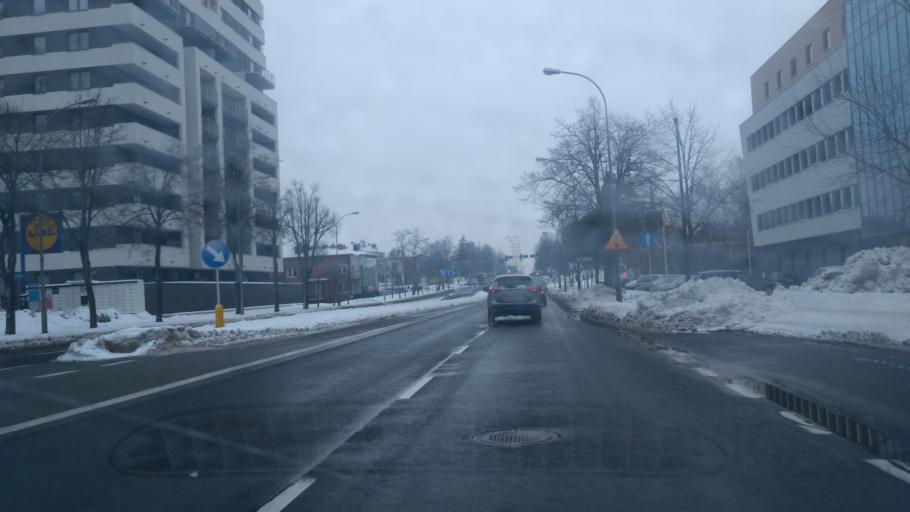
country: PL
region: Subcarpathian Voivodeship
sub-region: Rzeszow
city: Rzeszow
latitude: 50.0497
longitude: 22.0012
